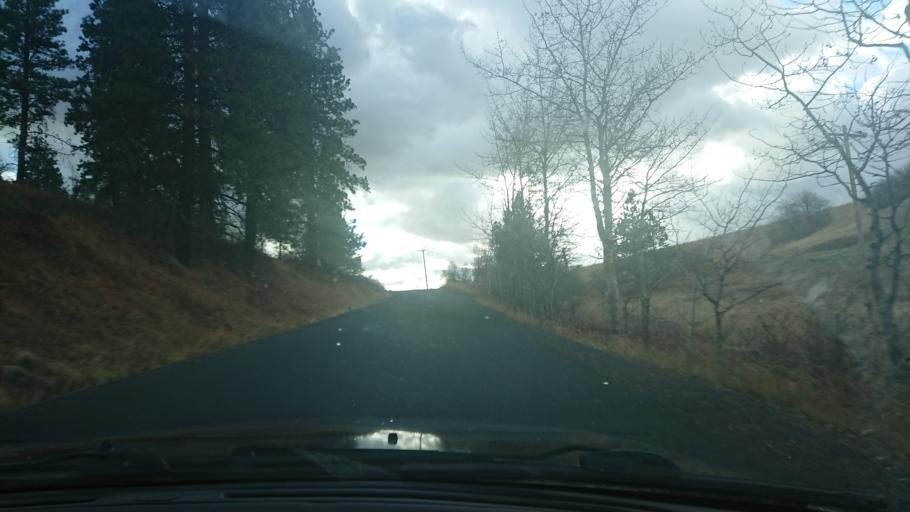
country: US
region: Idaho
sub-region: Latah County
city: Moscow
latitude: 46.6980
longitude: -116.8637
